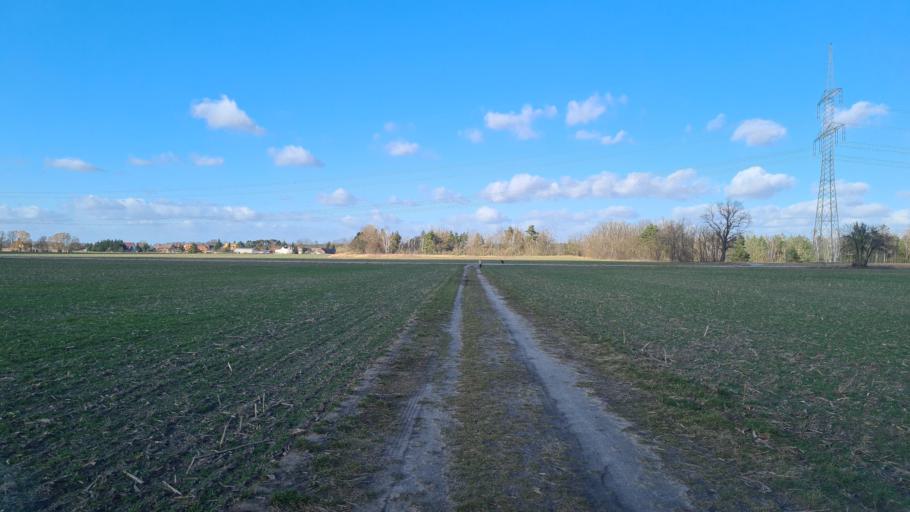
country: DE
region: Brandenburg
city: Finsterwalde
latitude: 51.6569
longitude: 13.6875
